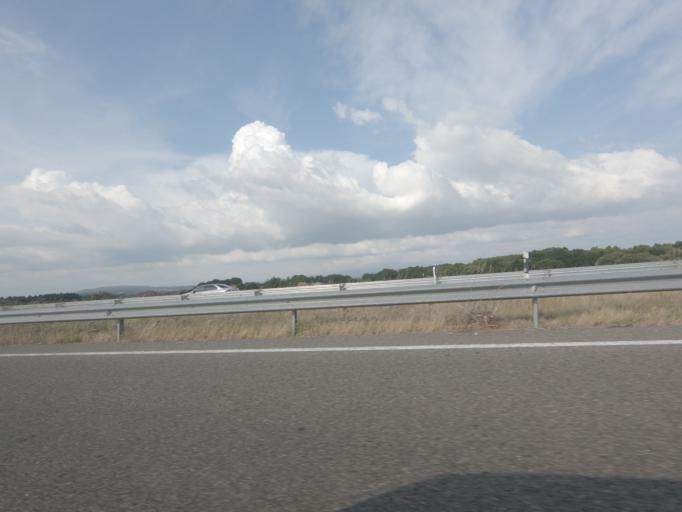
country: ES
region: Galicia
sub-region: Provincia de Ourense
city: Ambia
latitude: 42.1353
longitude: -7.7433
